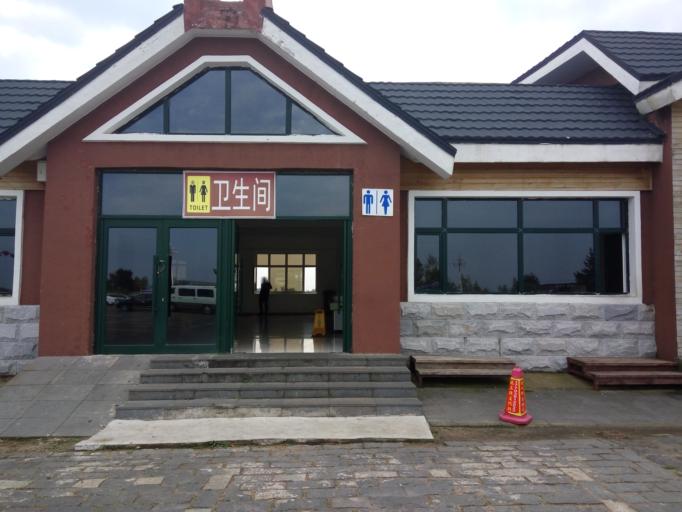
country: CN
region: Heilongjiang Sheng
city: Erjing
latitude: 48.6485
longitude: 126.1490
